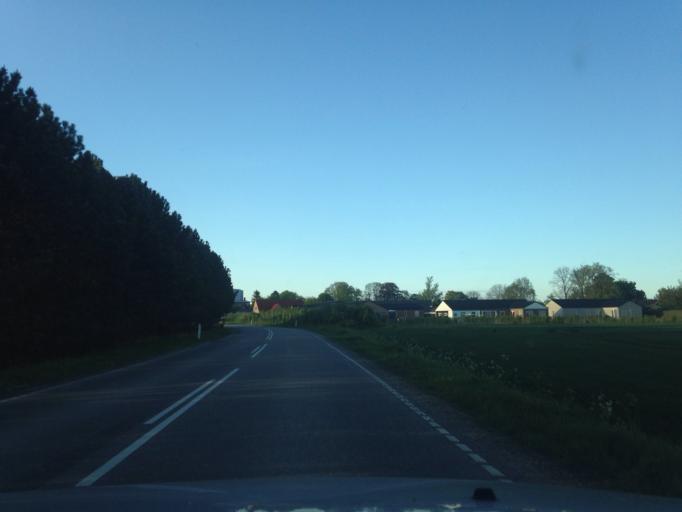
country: DK
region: Zealand
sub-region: Greve Kommune
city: Tune
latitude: 55.6132
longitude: 12.1855
